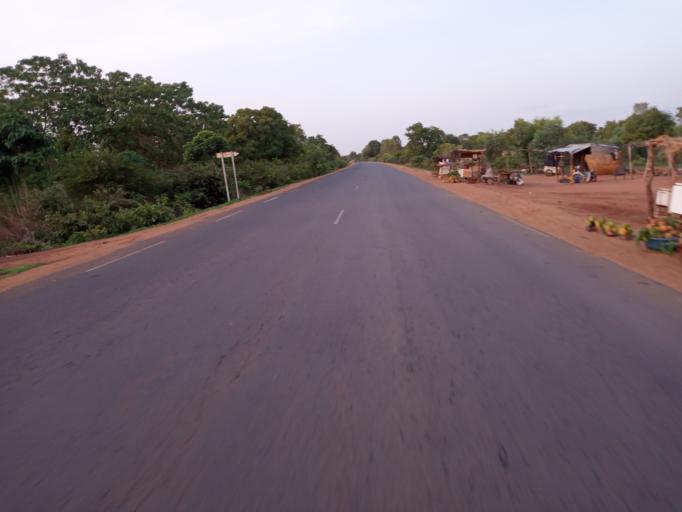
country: ML
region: Bamako
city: Bamako
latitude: 12.2872
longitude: -8.1732
